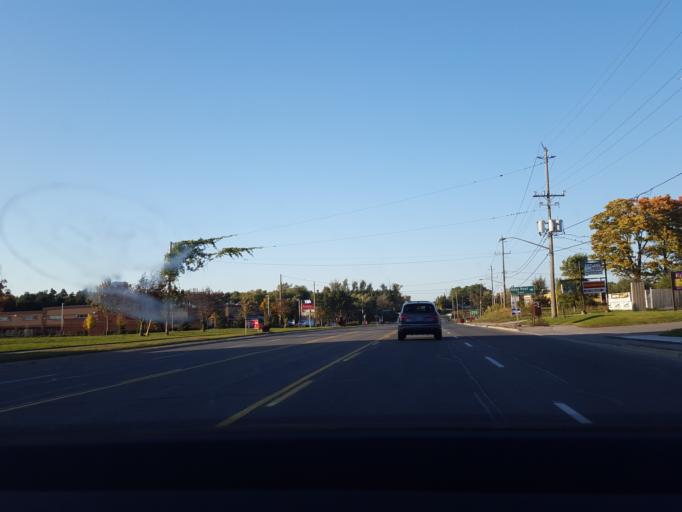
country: CA
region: Ontario
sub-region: York
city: Richmond Hill
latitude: 43.9526
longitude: -79.4565
